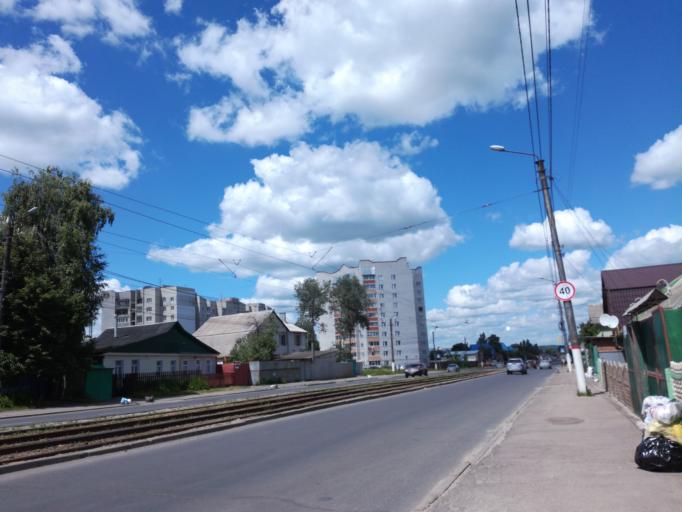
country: RU
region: Kursk
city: Kursk
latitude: 51.7496
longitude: 36.2457
